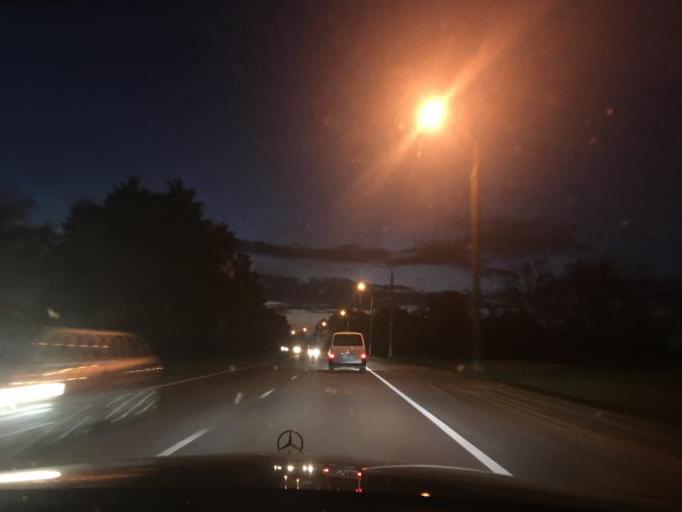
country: BY
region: Brest
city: Brest
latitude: 52.0585
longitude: 23.7148
